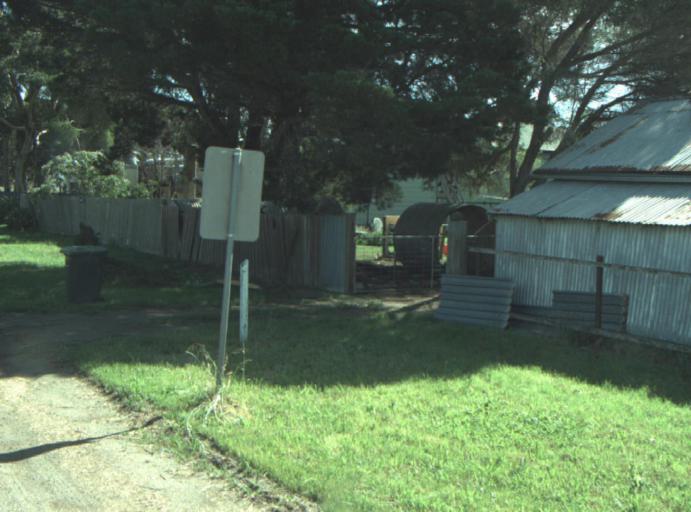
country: AU
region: Victoria
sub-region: Greater Geelong
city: Lara
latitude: -37.9970
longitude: 144.4198
